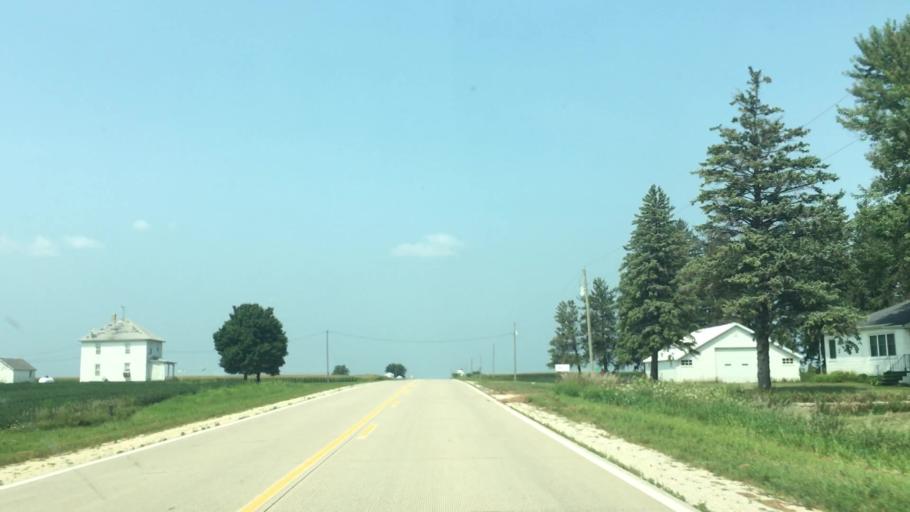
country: US
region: Iowa
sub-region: Fayette County
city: Oelwein
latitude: 42.7101
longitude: -91.8048
